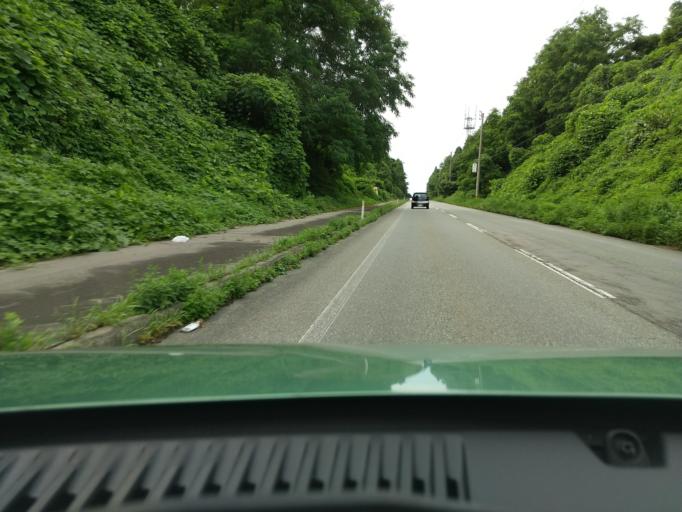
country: JP
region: Akita
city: Akita Shi
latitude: 39.8078
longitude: 140.0940
